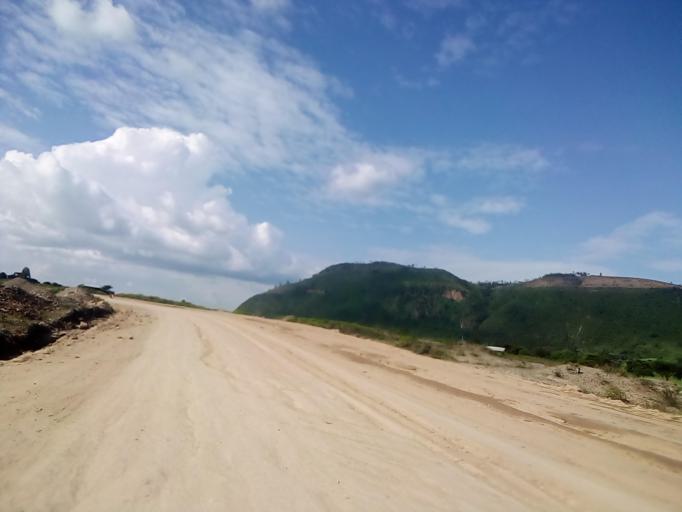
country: ET
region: Southern Nations, Nationalities, and People's Region
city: K'olito
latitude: 7.6277
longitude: 38.0638
